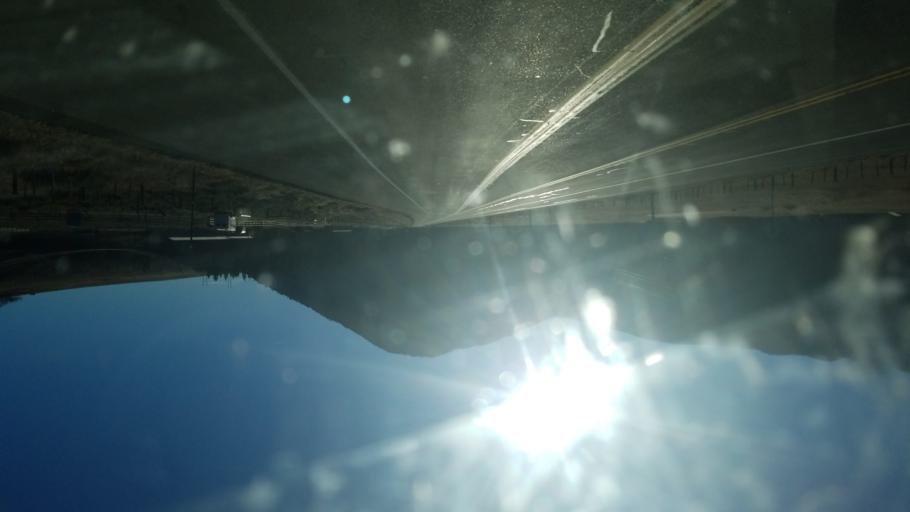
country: US
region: Colorado
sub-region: Gunnison County
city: Crested Butte
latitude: 38.8042
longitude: -106.8903
